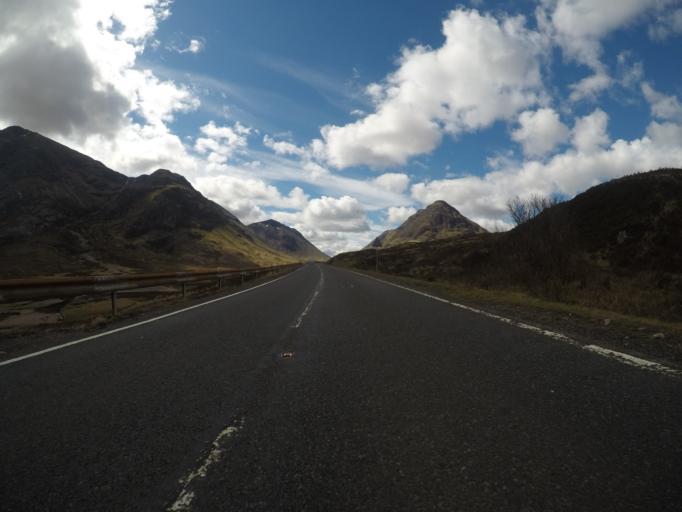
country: GB
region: Scotland
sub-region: Highland
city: Spean Bridge
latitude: 56.6639
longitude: -4.9081
